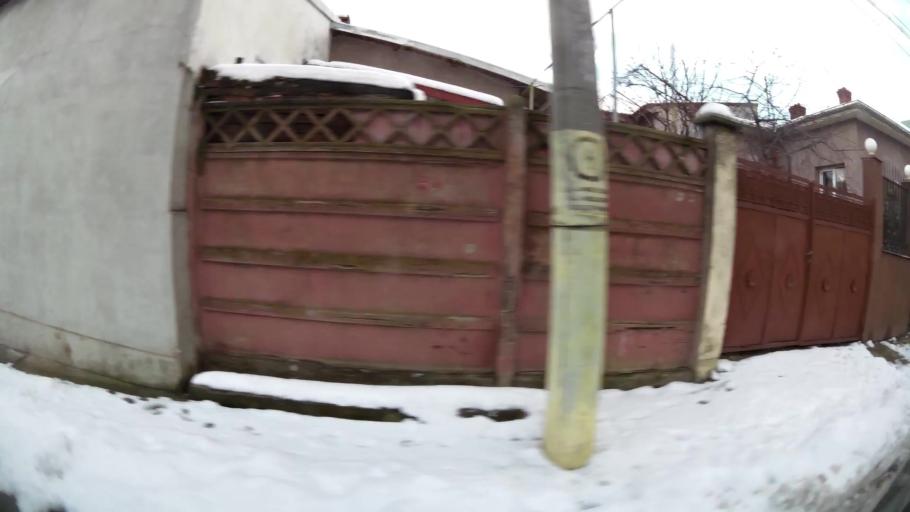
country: RO
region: Ilfov
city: Dobroesti
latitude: 44.4482
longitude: 26.1800
